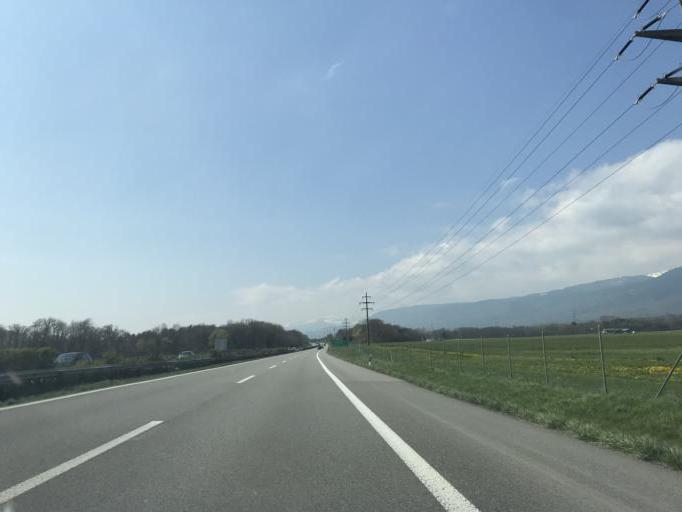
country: CH
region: Vaud
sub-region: Nyon District
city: Begnins
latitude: 46.4201
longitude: 6.2482
